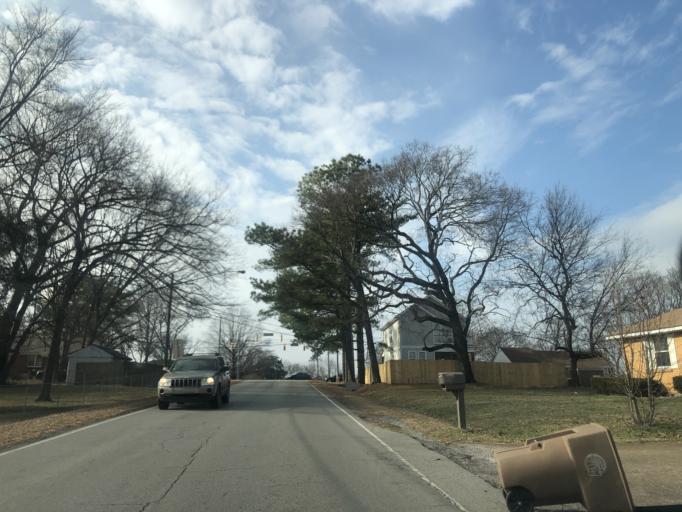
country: US
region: Tennessee
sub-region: Davidson County
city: Oak Hill
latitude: 36.1070
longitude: -86.7275
